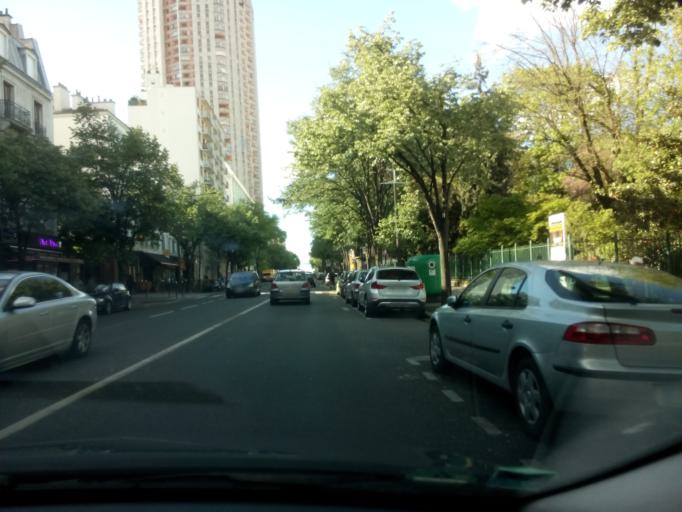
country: FR
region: Ile-de-France
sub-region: Departement du Val-de-Marne
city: Le Kremlin-Bicetre
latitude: 48.8277
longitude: 2.3587
